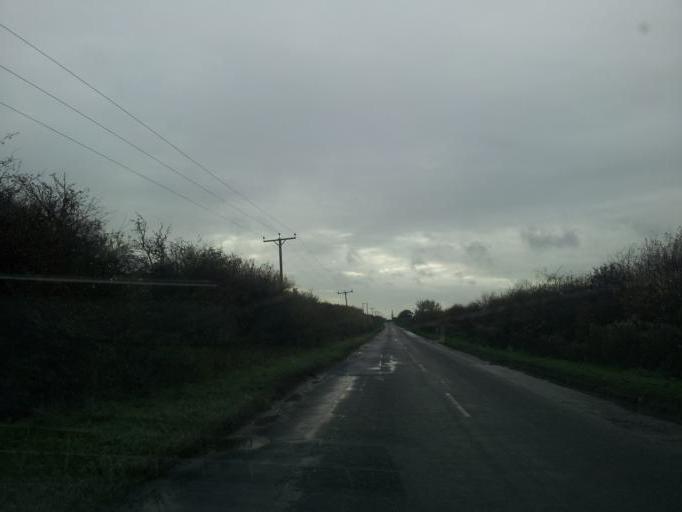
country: GB
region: England
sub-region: Nottinghamshire
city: Newark on Trent
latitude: 53.0416
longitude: -0.7972
